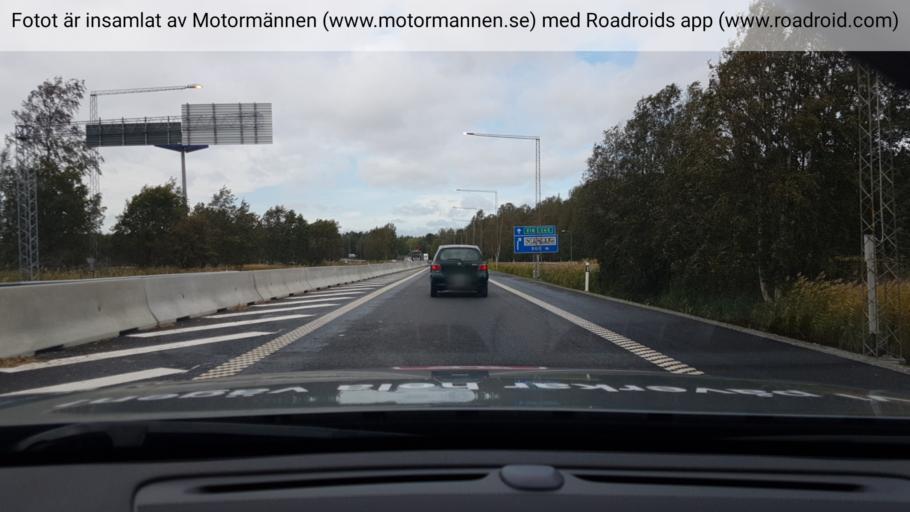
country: SE
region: Vaermland
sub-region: Hammaro Kommun
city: Skoghall
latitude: 59.3807
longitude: 13.4207
